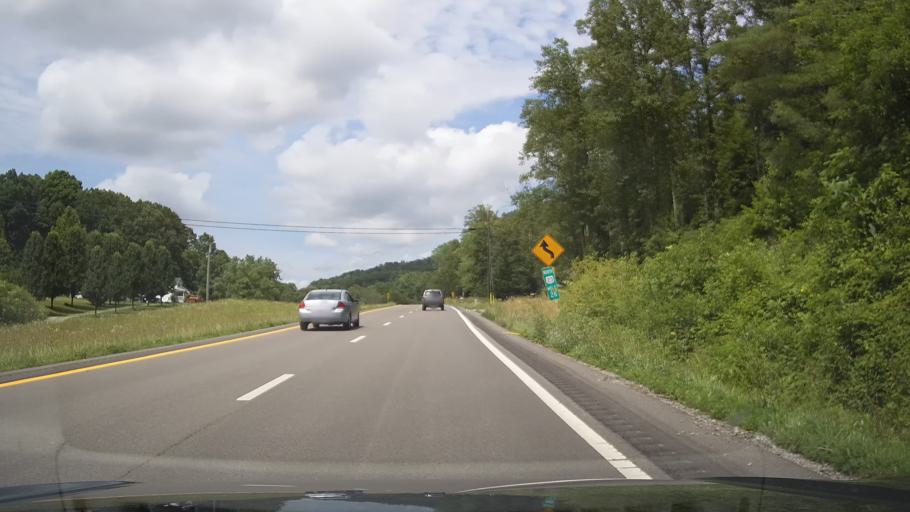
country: US
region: Virginia
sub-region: Lee County
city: Dryden
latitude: 36.7742
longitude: -82.8235
